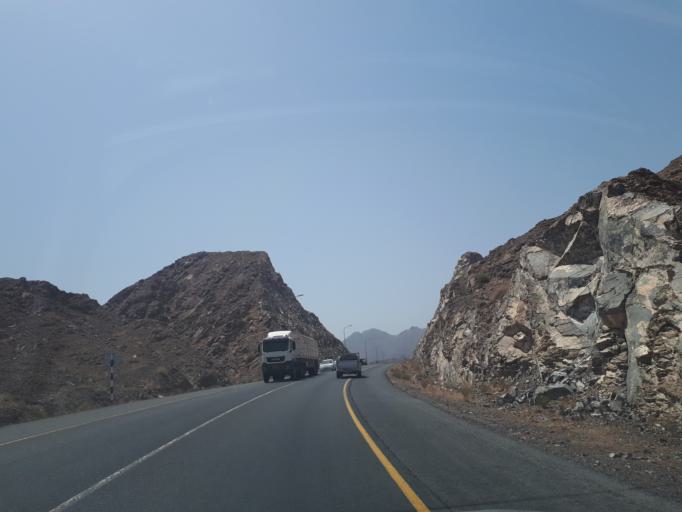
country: OM
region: Muhafazat ad Dakhiliyah
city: Sufalat Sama'il
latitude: 23.1984
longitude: 58.0845
